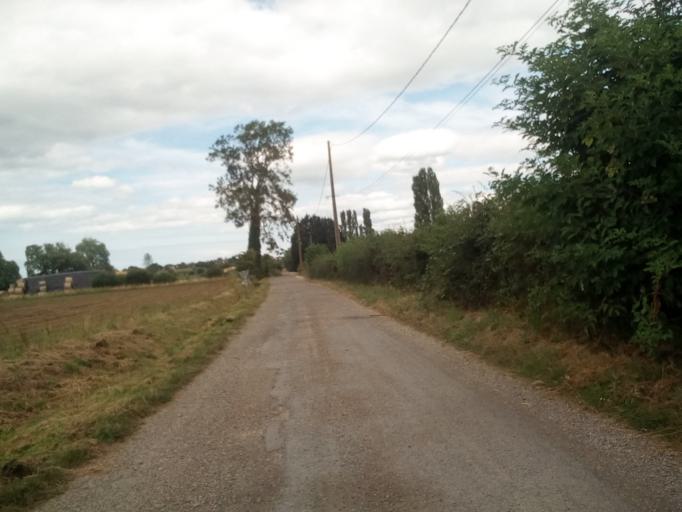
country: FR
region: Lower Normandy
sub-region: Departement du Calvados
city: Troarn
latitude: 49.1726
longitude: -0.1666
